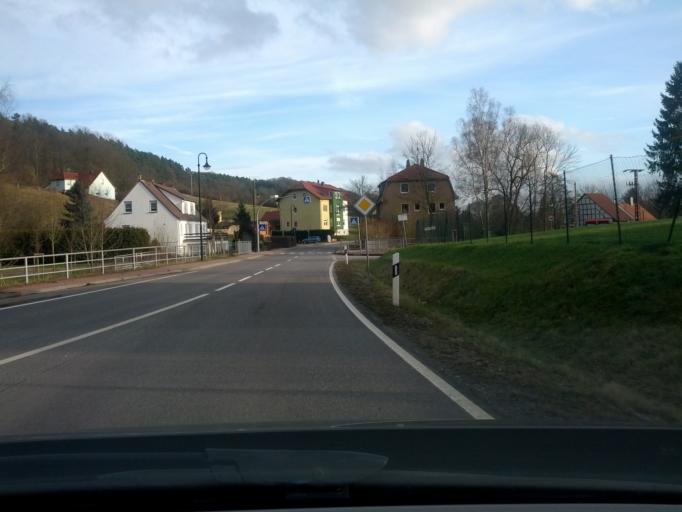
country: DE
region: Thuringia
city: Ifta
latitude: 51.0690
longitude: 10.1702
